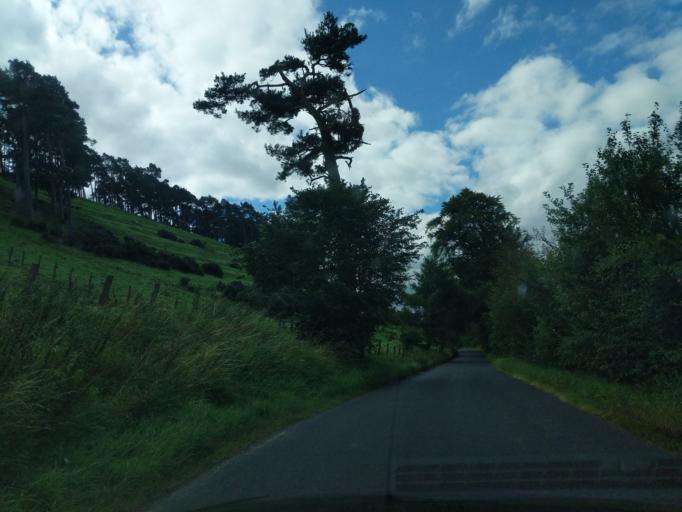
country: GB
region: Scotland
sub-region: The Scottish Borders
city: West Linton
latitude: 55.7106
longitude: -3.3349
